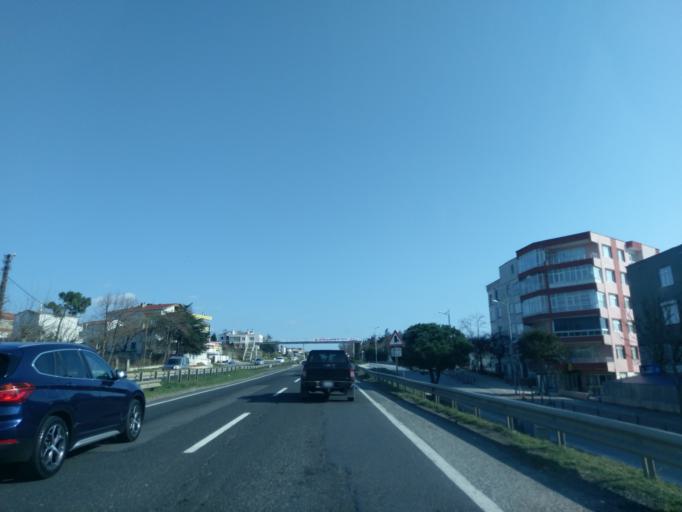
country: TR
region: Istanbul
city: Kumburgaz
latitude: 41.0229
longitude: 28.4730
